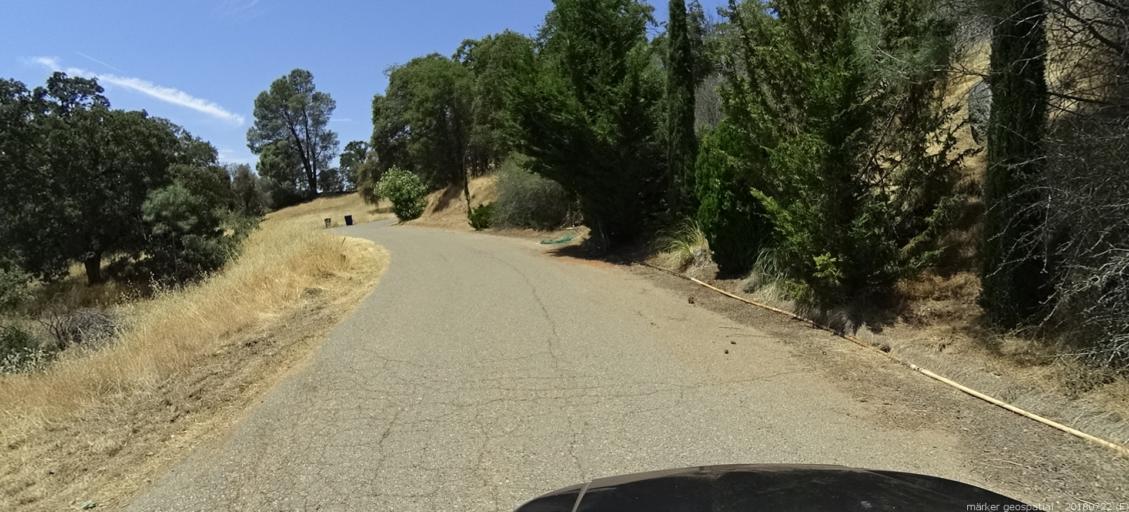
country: US
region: California
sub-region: Madera County
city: Coarsegold
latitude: 37.2453
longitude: -119.7354
